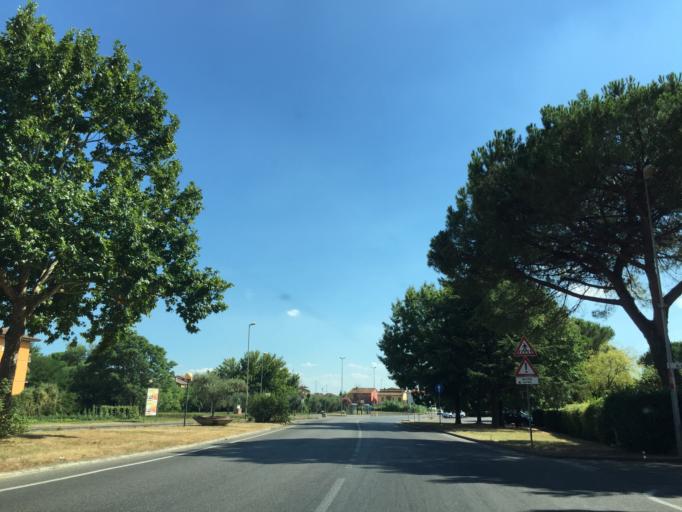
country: IT
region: Tuscany
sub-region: Provincia di Pistoia
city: Monsummano Terme
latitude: 43.8768
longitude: 10.8121
